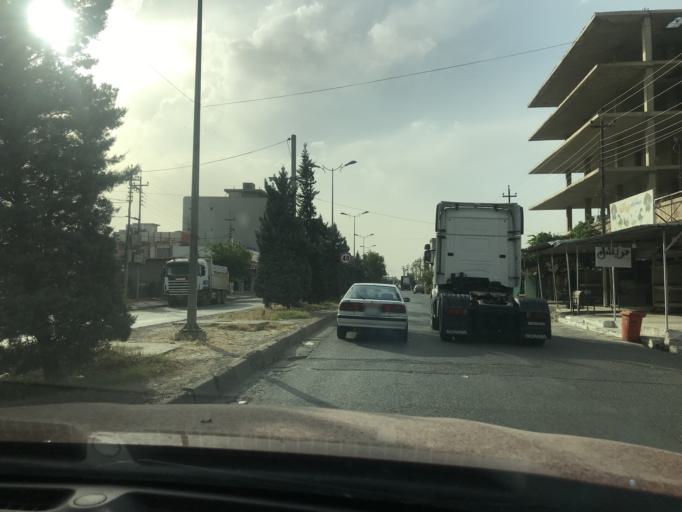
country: IQ
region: Arbil
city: Erbil
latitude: 36.1779
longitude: 43.9799
